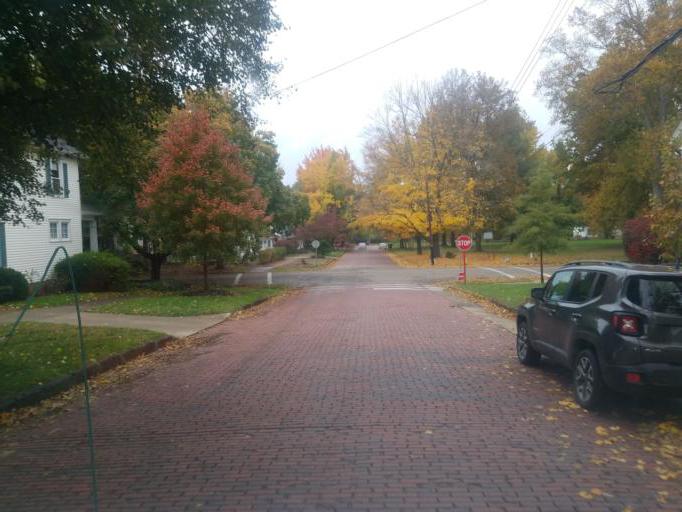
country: US
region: Ohio
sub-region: Washington County
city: Marietta
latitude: 39.4252
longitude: -81.4597
